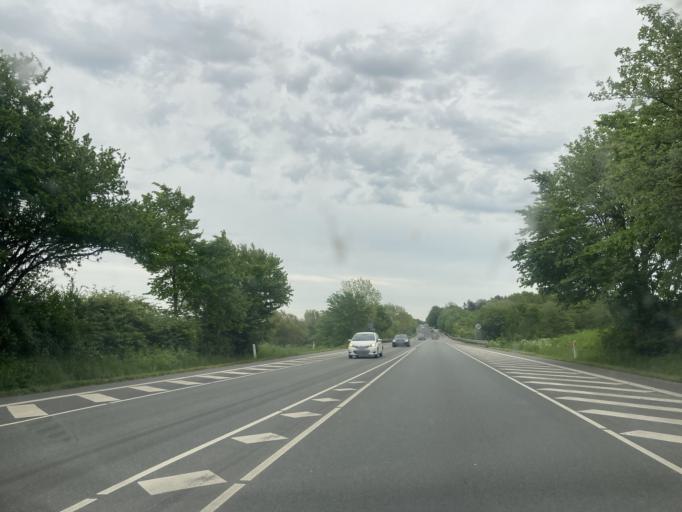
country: DK
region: Zealand
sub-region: Roskilde Kommune
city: Svogerslev
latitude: 55.6344
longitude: 11.9909
